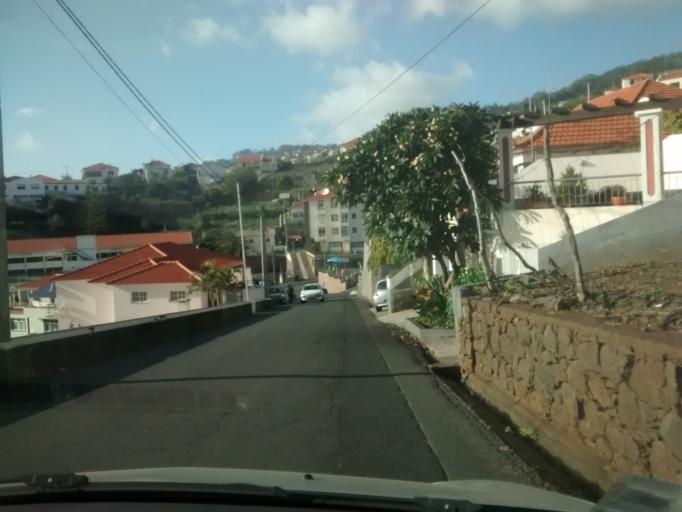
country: PT
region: Madeira
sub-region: Calheta
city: Estreito da Calheta
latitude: 32.7311
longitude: -17.1750
